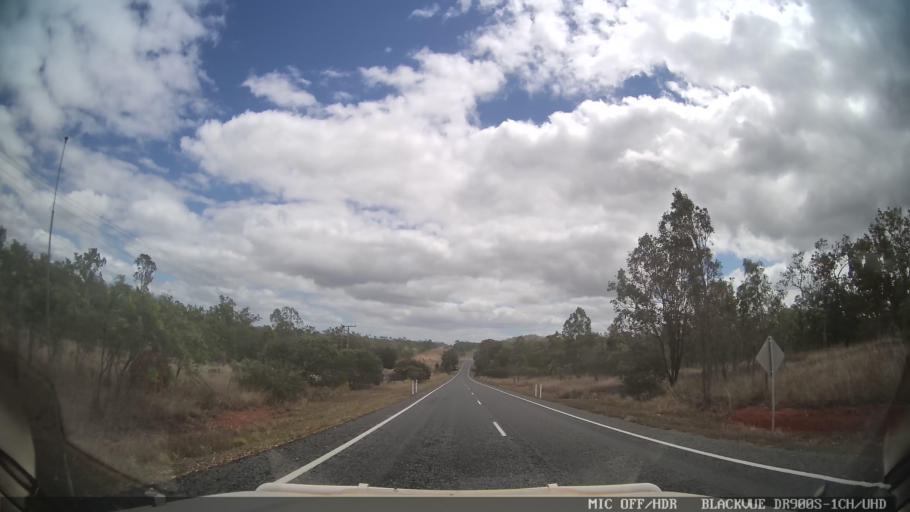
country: AU
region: Queensland
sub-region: Tablelands
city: Ravenshoe
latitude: -17.6985
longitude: 145.1999
